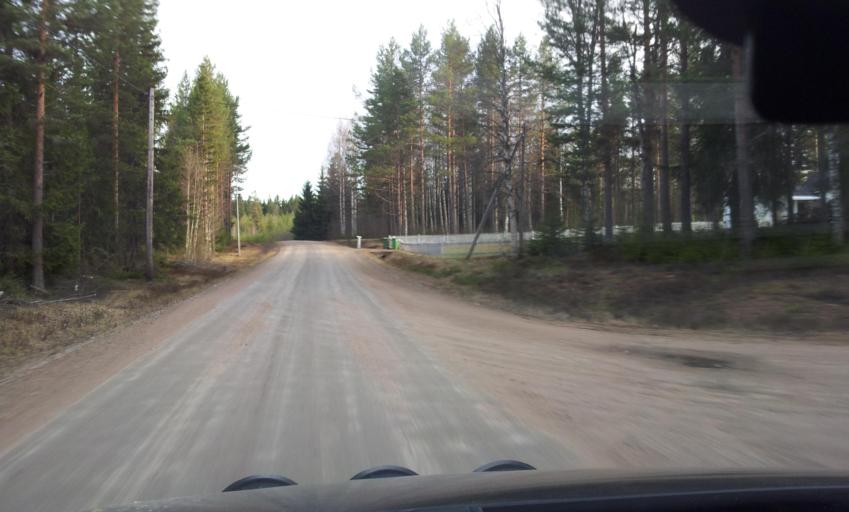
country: SE
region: Gaevleborg
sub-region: Ljusdals Kommun
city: Farila
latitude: 62.1356
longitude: 15.6613
